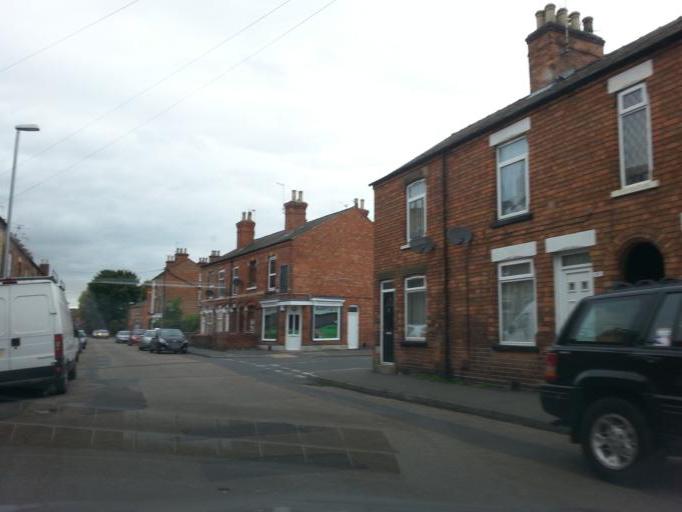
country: GB
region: England
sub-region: Nottinghamshire
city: Newark on Trent
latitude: 53.0727
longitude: -0.7973
